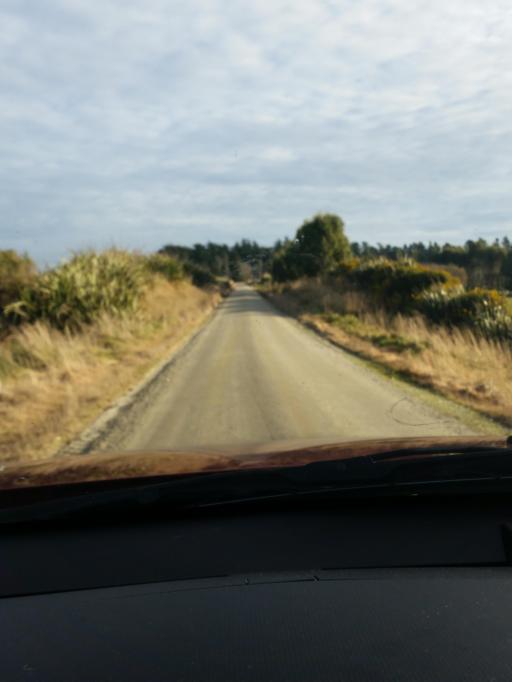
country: NZ
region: Southland
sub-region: Gore District
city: Gore
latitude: -46.2341
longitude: 168.7695
